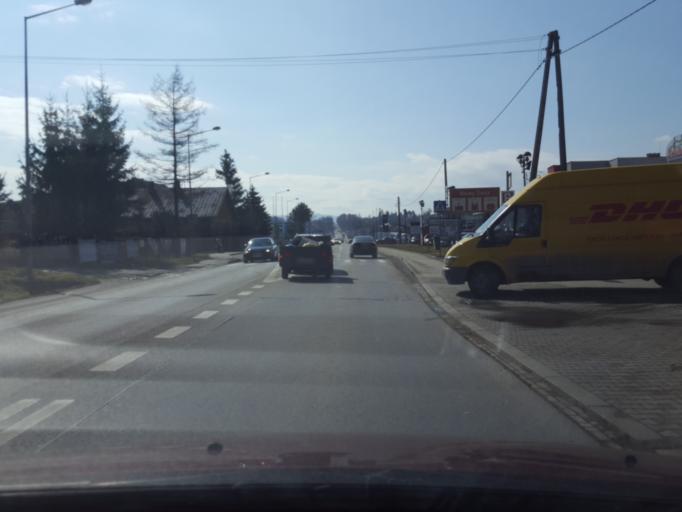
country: PL
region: Lesser Poland Voivodeship
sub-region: Powiat nowosadecki
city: Nowy Sacz
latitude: 49.6566
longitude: 20.6897
